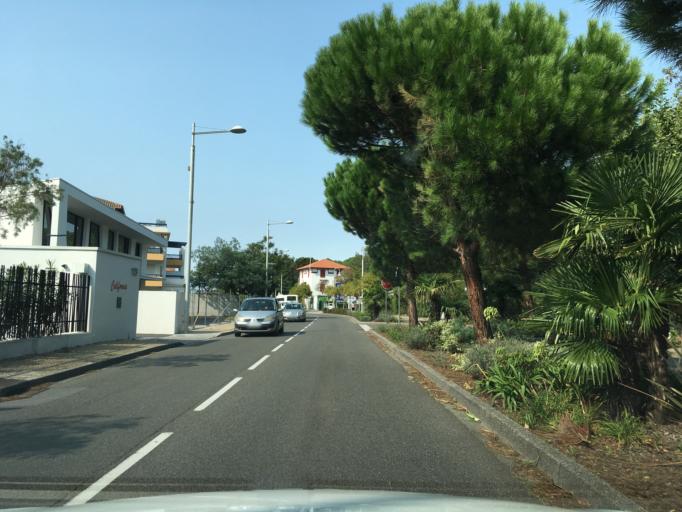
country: FR
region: Aquitaine
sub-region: Departement des Pyrenees-Atlantiques
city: Bayonne
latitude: 43.5124
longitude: -1.5001
